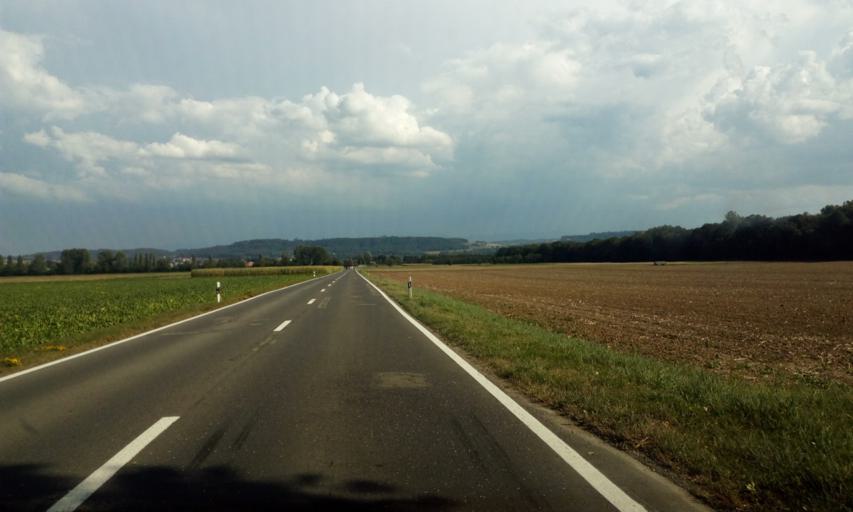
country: CH
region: Fribourg
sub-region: Broye District
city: Domdidier
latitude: 46.8978
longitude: 6.9965
